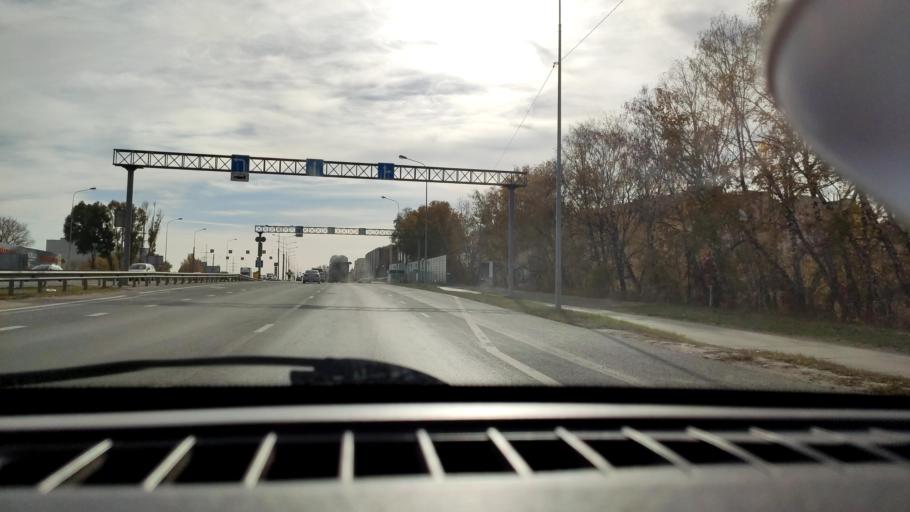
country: RU
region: Samara
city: Petra-Dubrava
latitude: 53.3124
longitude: 50.2920
